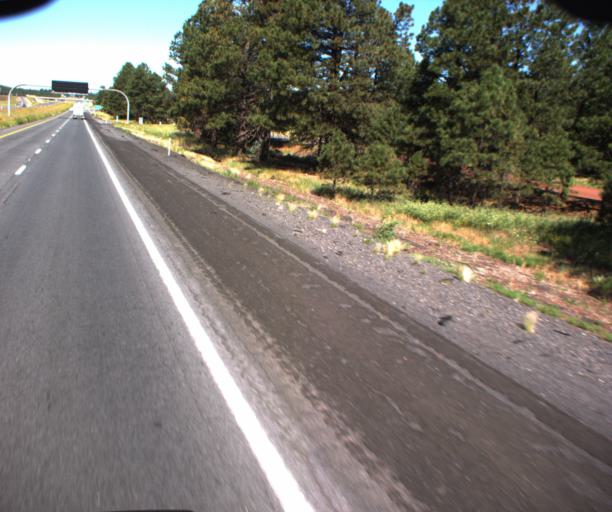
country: US
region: Arizona
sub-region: Coconino County
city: Williams
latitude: 35.2585
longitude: -112.1121
